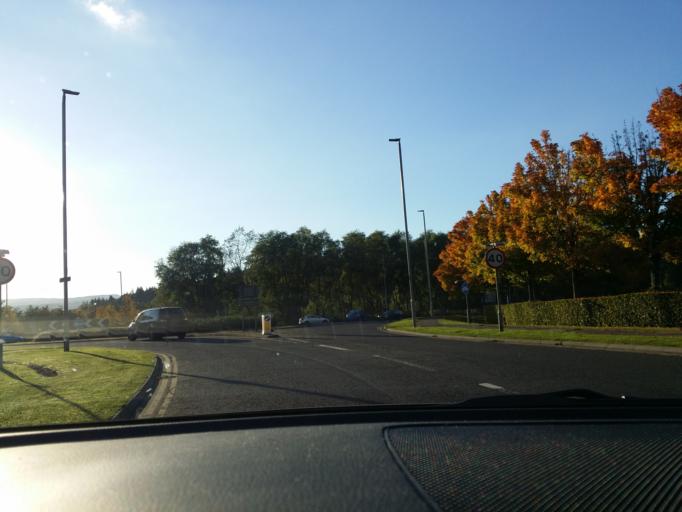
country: GB
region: Scotland
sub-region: Stirling
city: Stirling
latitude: 56.1300
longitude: -3.9634
